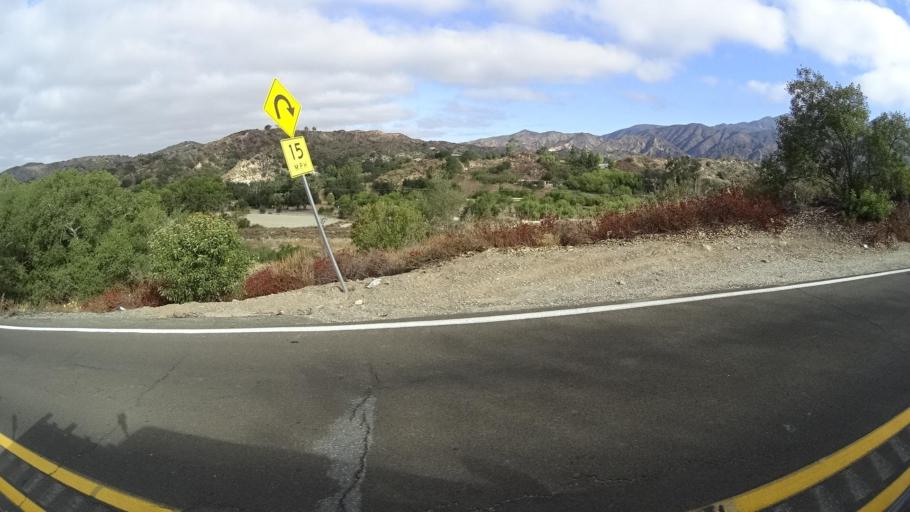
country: US
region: California
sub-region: Orange County
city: Trabuco Canyon
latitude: 33.6572
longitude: -117.5838
